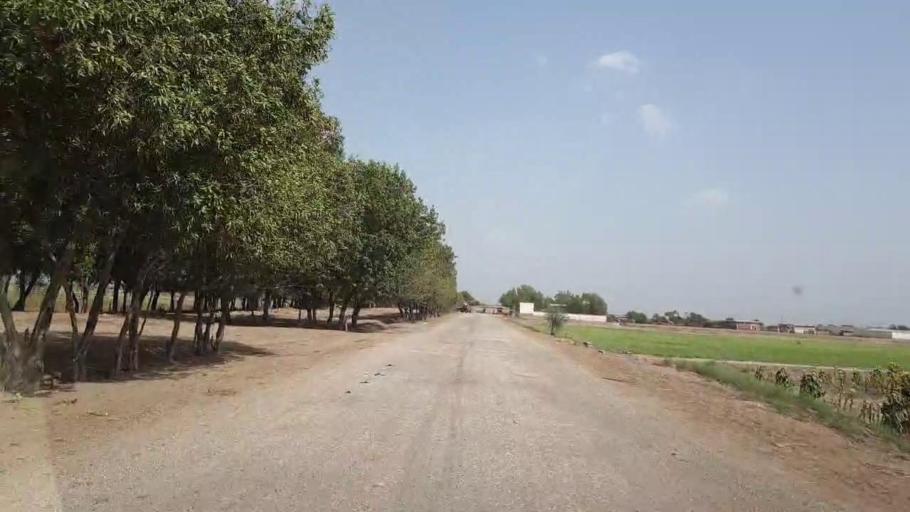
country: PK
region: Sindh
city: Rajo Khanani
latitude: 25.0497
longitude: 68.8744
